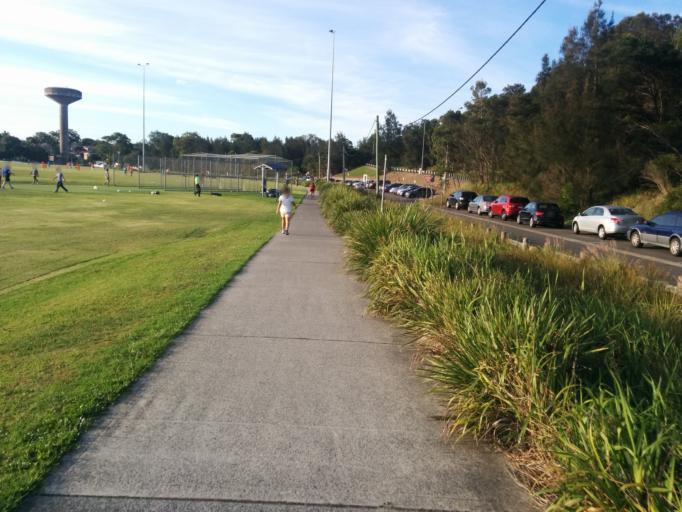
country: AU
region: New South Wales
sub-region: Rockdale
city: Arncliffe
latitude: -33.9295
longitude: 151.1628
